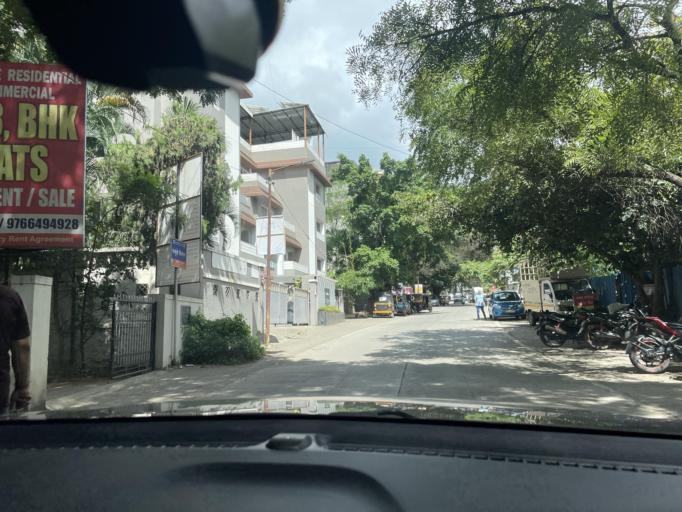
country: IN
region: Maharashtra
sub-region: Pune Division
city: Shivaji Nagar
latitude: 18.5155
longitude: 73.7802
